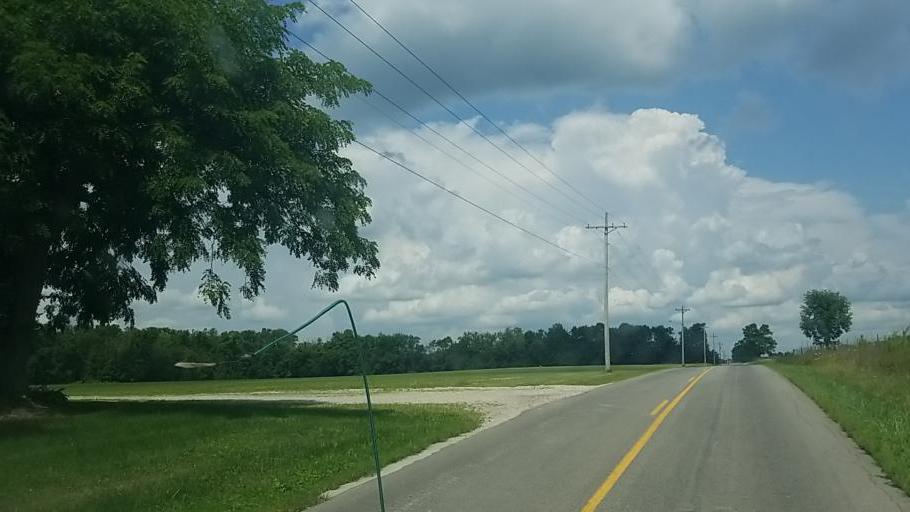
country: US
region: Ohio
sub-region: Medina County
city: Lodi
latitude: 41.0512
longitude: -82.0769
